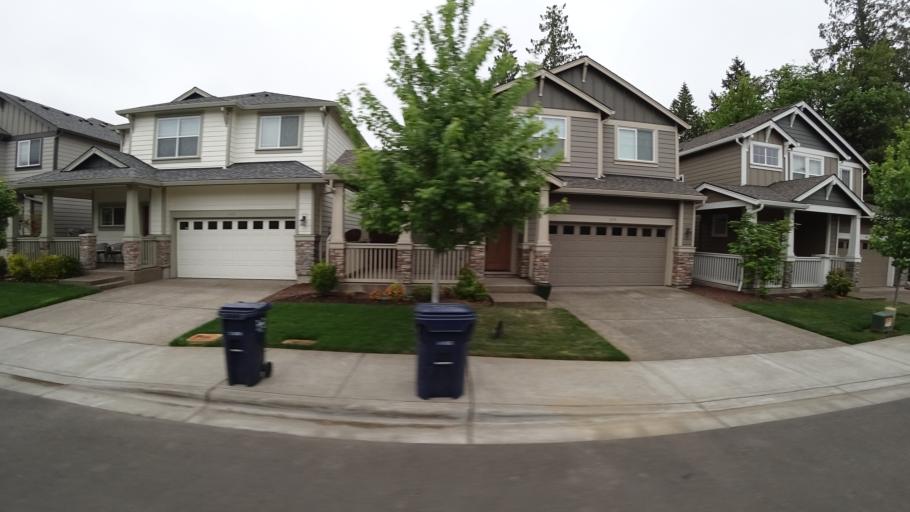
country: US
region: Oregon
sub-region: Washington County
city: Aloha
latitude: 45.5165
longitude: -122.8811
